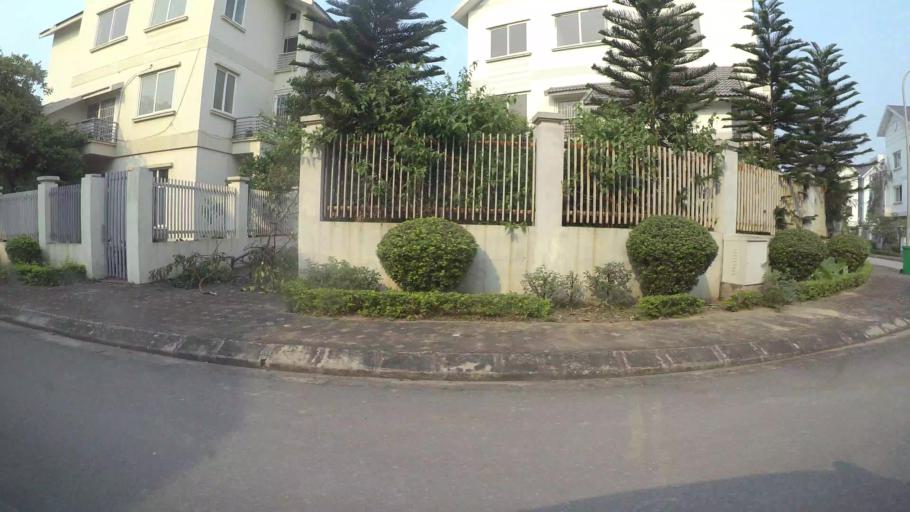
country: VN
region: Ha Noi
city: Ha Dong
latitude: 20.9976
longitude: 105.7455
